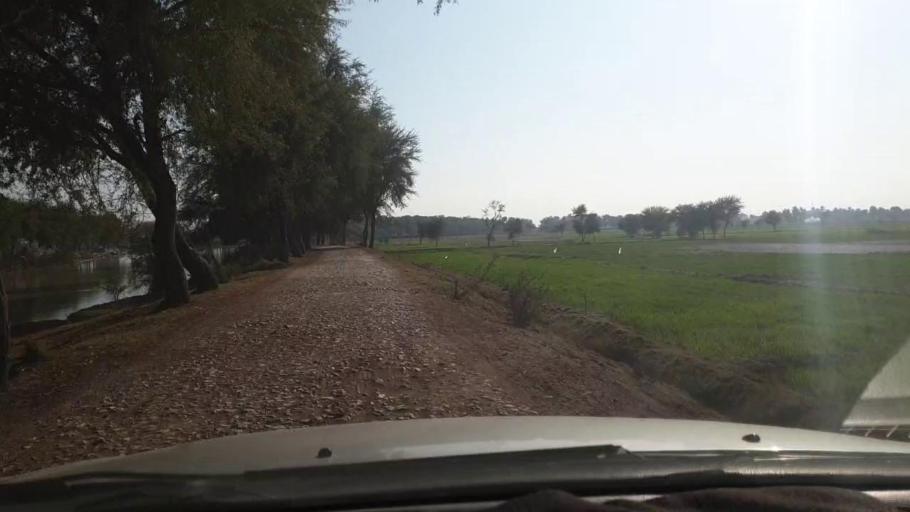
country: PK
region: Sindh
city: Mirpur Mathelo
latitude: 27.9892
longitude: 69.5447
